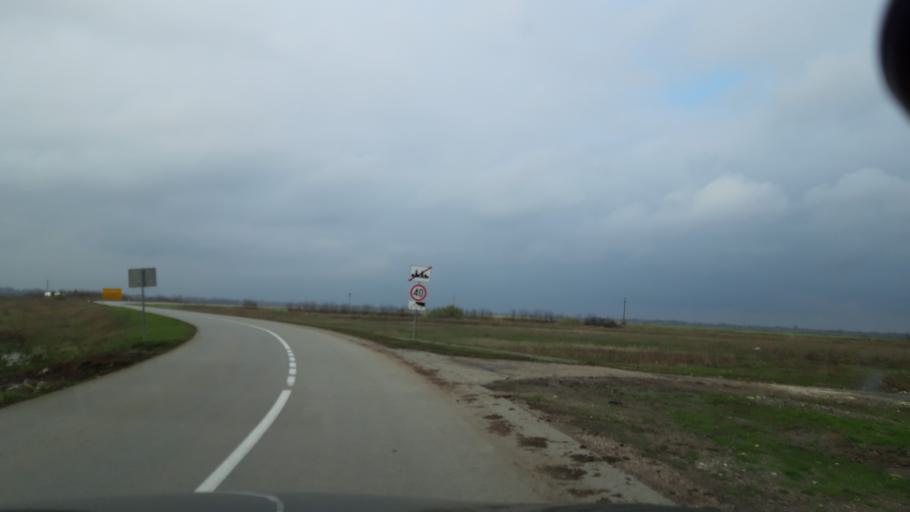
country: RS
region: Autonomna Pokrajina Vojvodina
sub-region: Severnobanatski Okrug
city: Kanjiza
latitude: 46.1305
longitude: 20.0937
